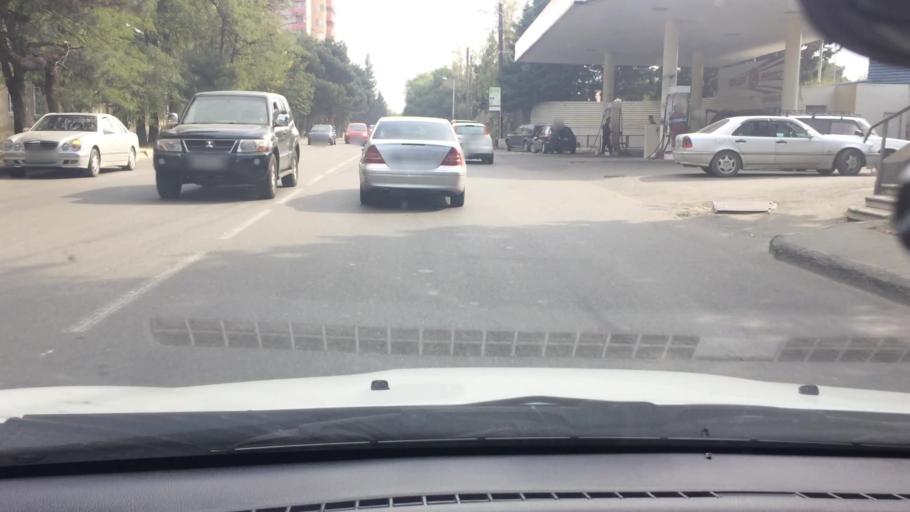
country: GE
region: T'bilisi
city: Tbilisi
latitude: 41.6502
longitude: 44.9079
